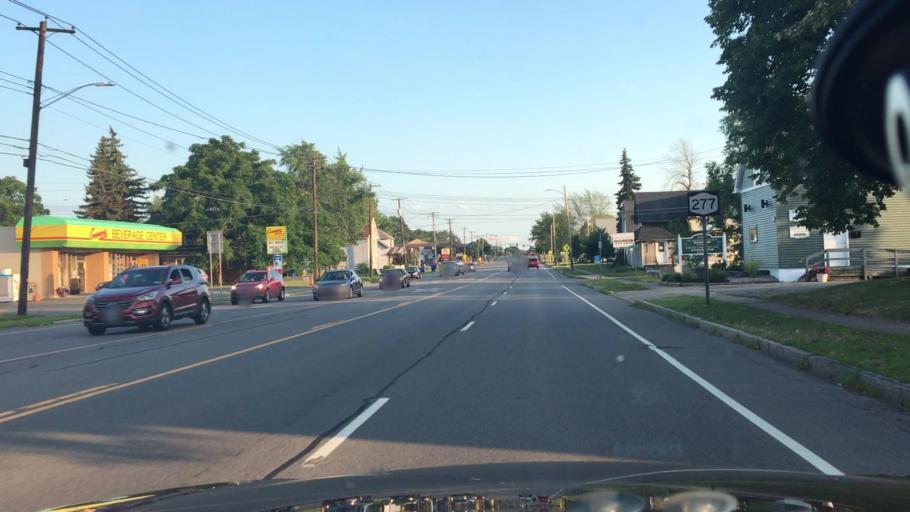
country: US
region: New York
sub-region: Erie County
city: West Seneca
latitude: 42.8381
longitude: -78.7541
